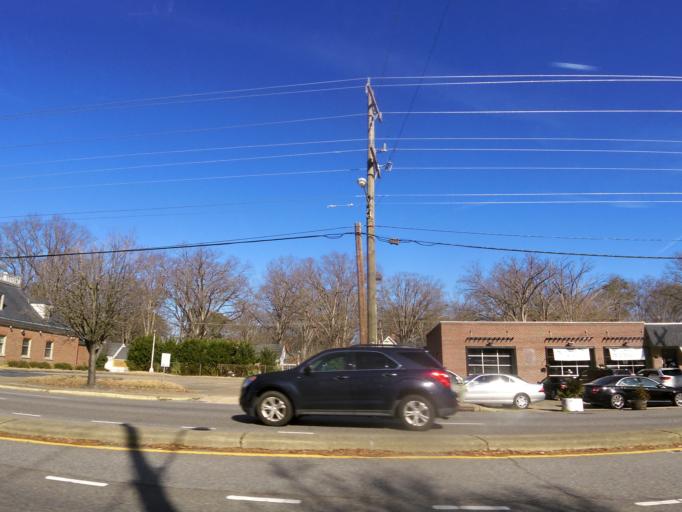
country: US
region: Virginia
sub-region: City of Newport News
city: Newport News
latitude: 37.0346
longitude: -76.4638
